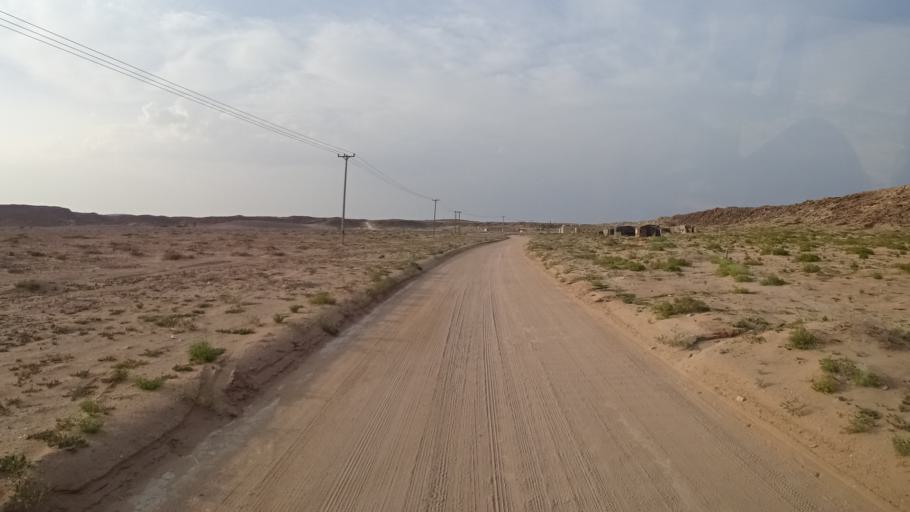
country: OM
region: Ash Sharqiyah
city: Sur
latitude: 22.4450
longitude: 59.8270
